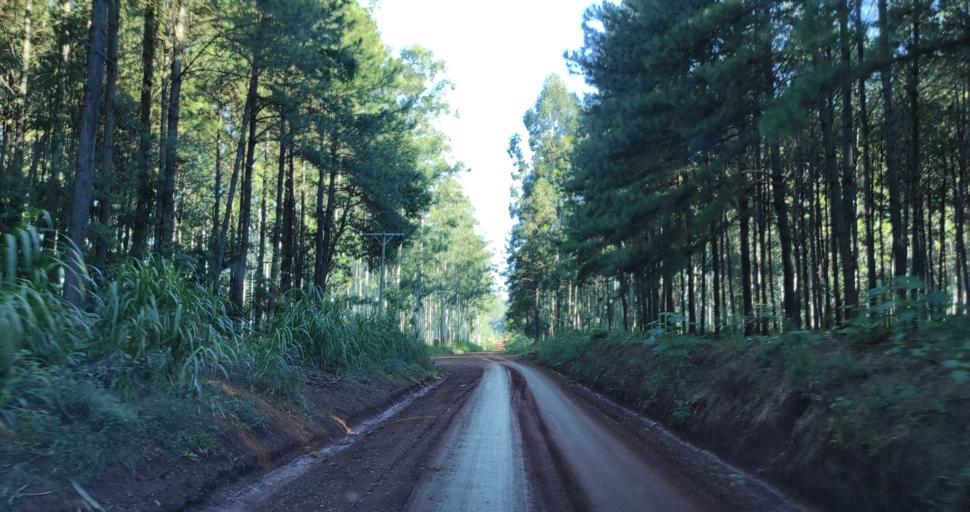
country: AR
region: Misiones
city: Puerto Rico
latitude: -26.8612
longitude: -55.0147
